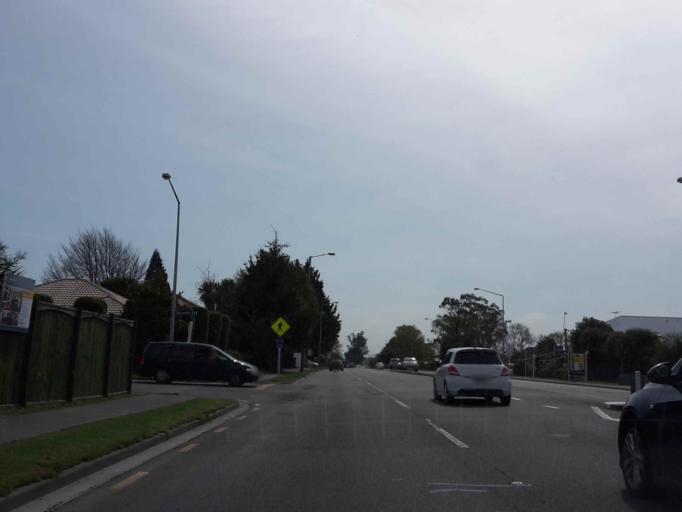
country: NZ
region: Canterbury
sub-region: Waimakariri District
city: Kaiapoi
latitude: -43.4442
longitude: 172.6329
